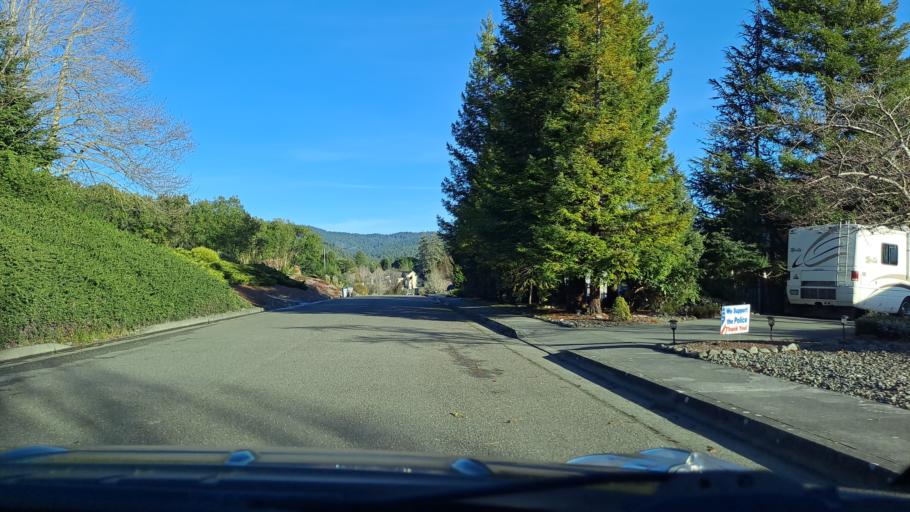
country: US
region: California
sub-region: Humboldt County
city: Fortuna
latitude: 40.5987
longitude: -124.1368
